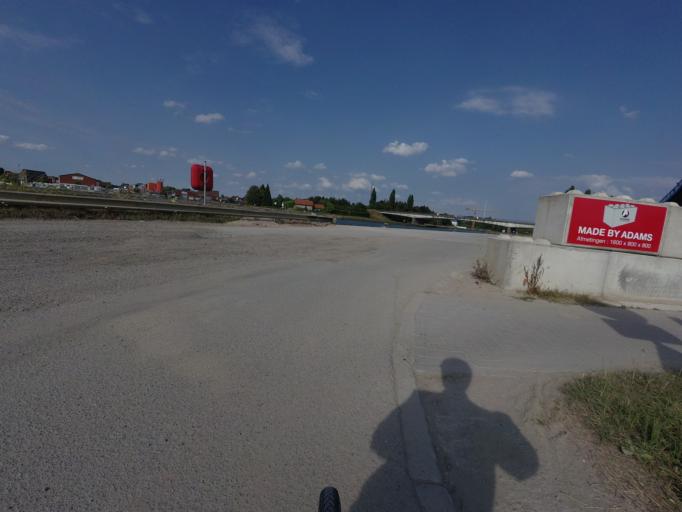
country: BE
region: Flanders
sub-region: Provincie Antwerpen
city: Zandhoven
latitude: 51.1959
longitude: 4.6389
